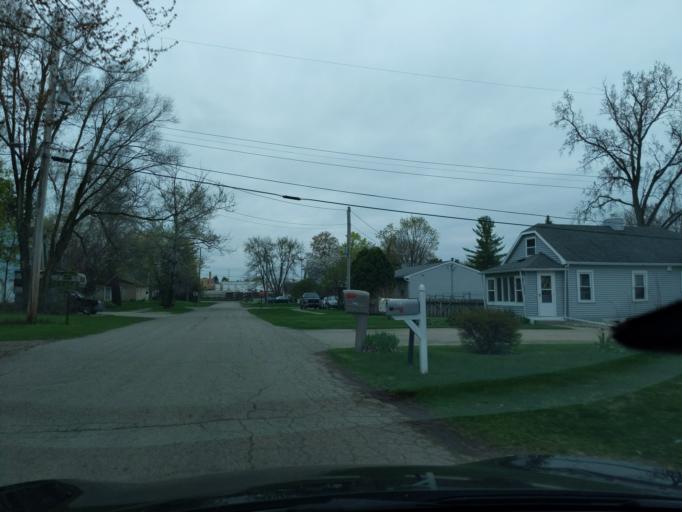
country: US
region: Michigan
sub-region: Ingham County
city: Edgemont Park
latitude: 42.7309
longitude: -84.5844
